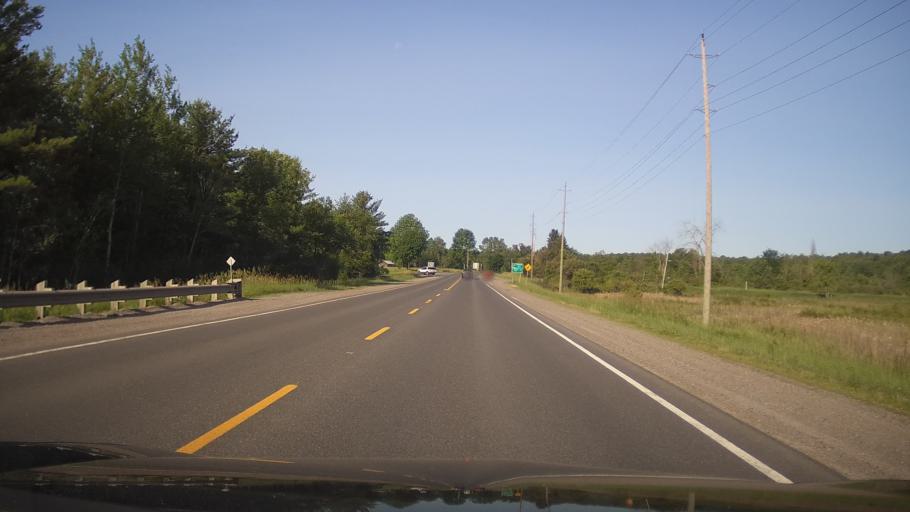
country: CA
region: Ontario
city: Quinte West
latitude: 44.5062
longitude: -77.4932
